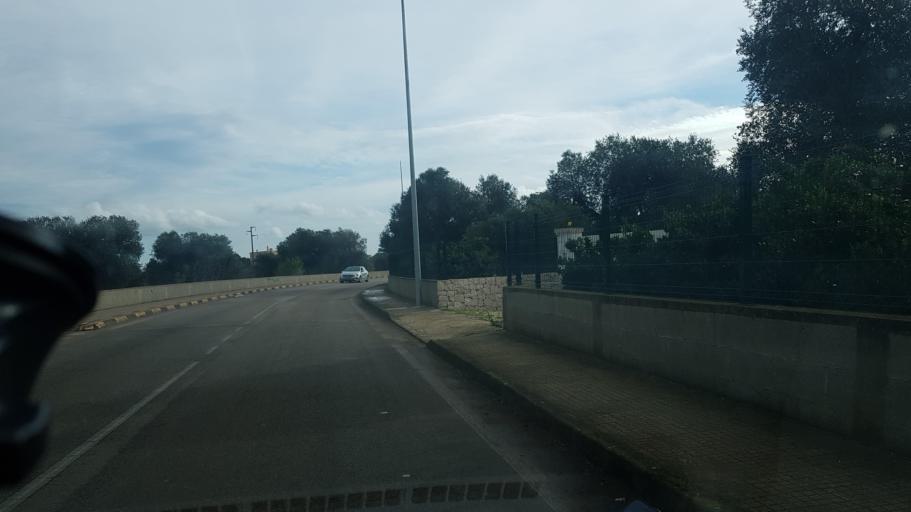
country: IT
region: Apulia
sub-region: Provincia di Brindisi
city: San Vito dei Normanni
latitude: 40.6648
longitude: 17.7130
